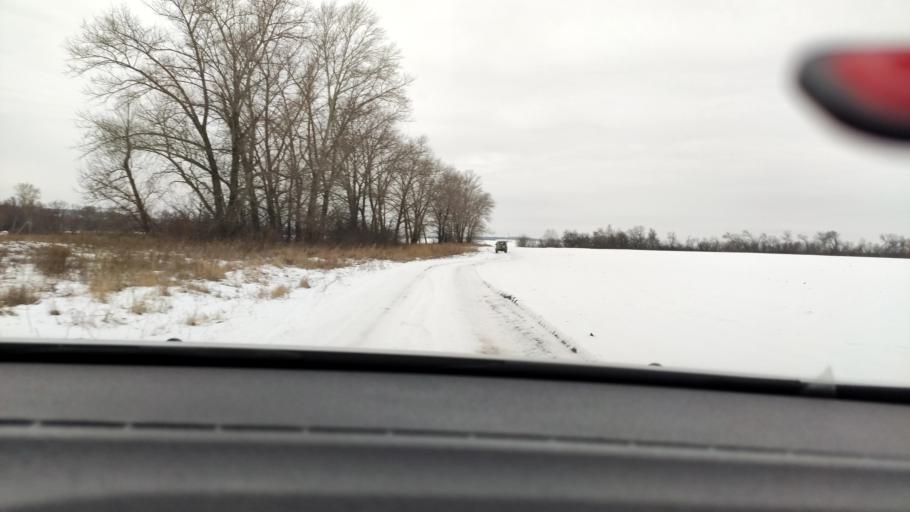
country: RU
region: Voronezj
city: Semiluki
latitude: 51.7053
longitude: 38.9760
